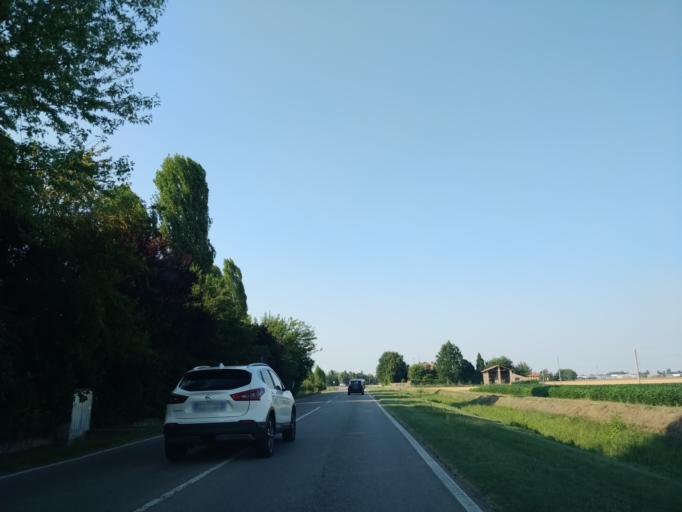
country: IT
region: Emilia-Romagna
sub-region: Provincia di Bologna
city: Argelato
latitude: 44.6225
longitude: 11.3368
